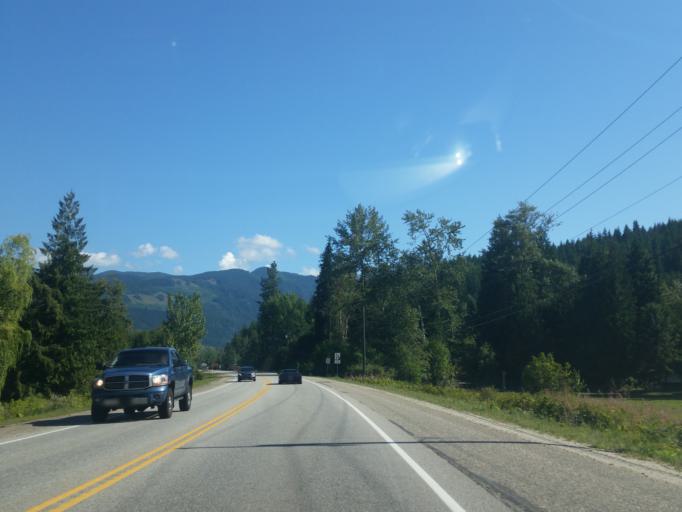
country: CA
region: British Columbia
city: Sicamous
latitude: 50.8506
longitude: -118.9467
